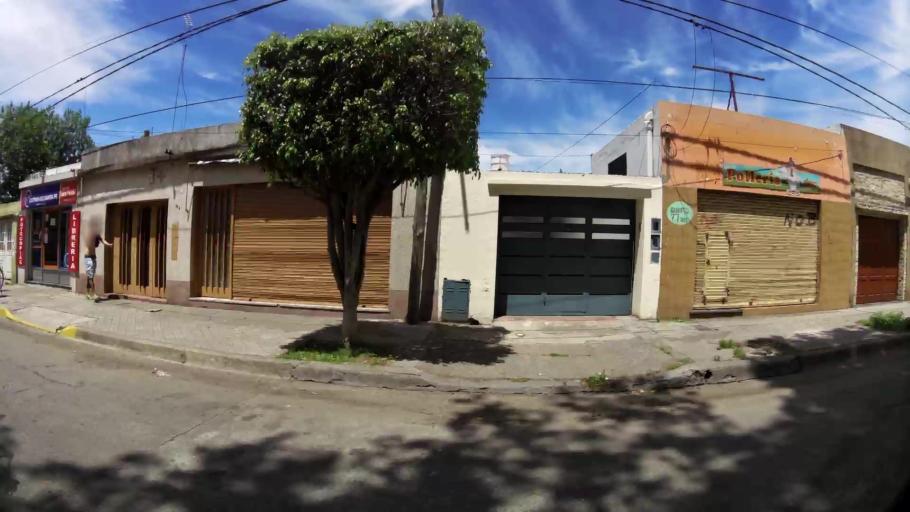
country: AR
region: Santa Fe
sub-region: Departamento de Rosario
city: Rosario
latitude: -32.9764
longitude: -60.6287
